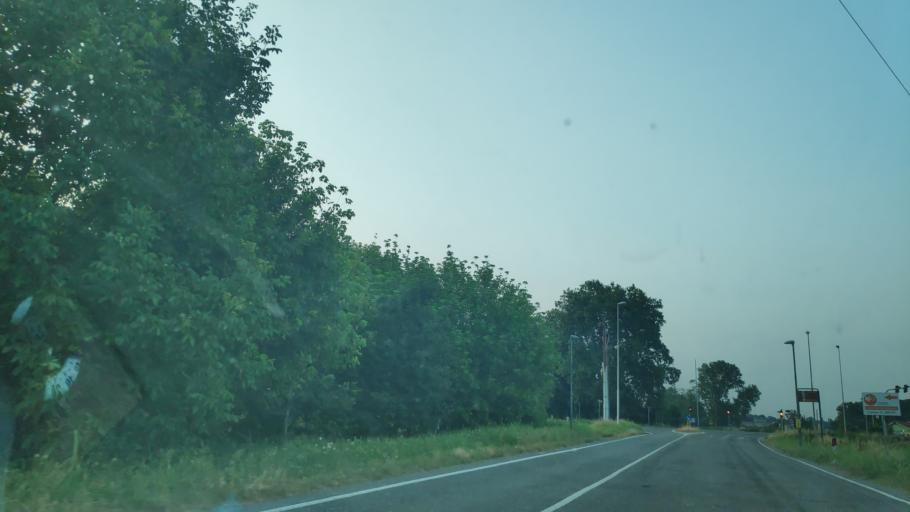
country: IT
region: Lombardy
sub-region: Citta metropolitana di Milano
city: Paullo
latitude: 45.4245
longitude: 9.4032
